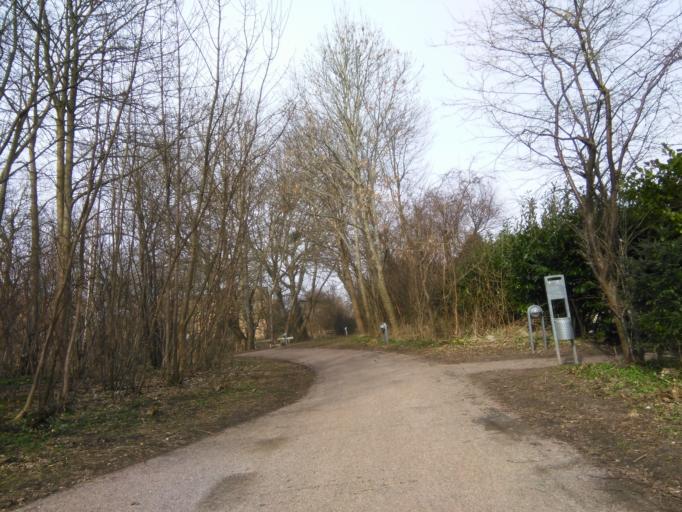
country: DK
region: Central Jutland
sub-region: Arhus Kommune
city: Beder
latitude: 56.1052
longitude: 10.2217
